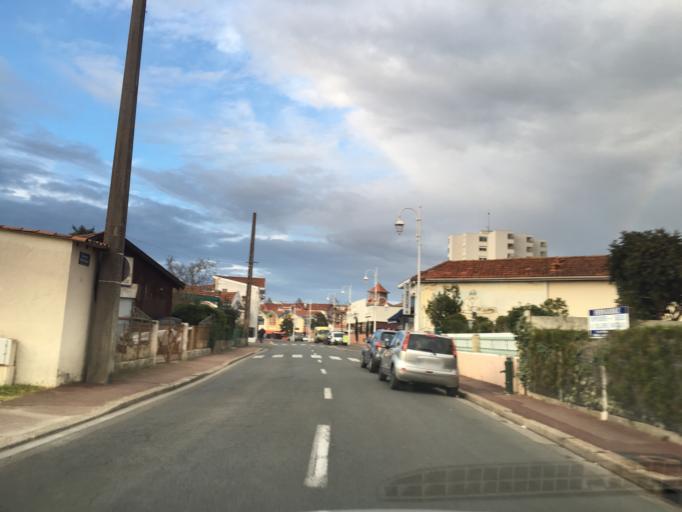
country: FR
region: Aquitaine
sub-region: Departement de la Gironde
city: Arcachon
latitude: 44.6551
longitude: -1.1465
